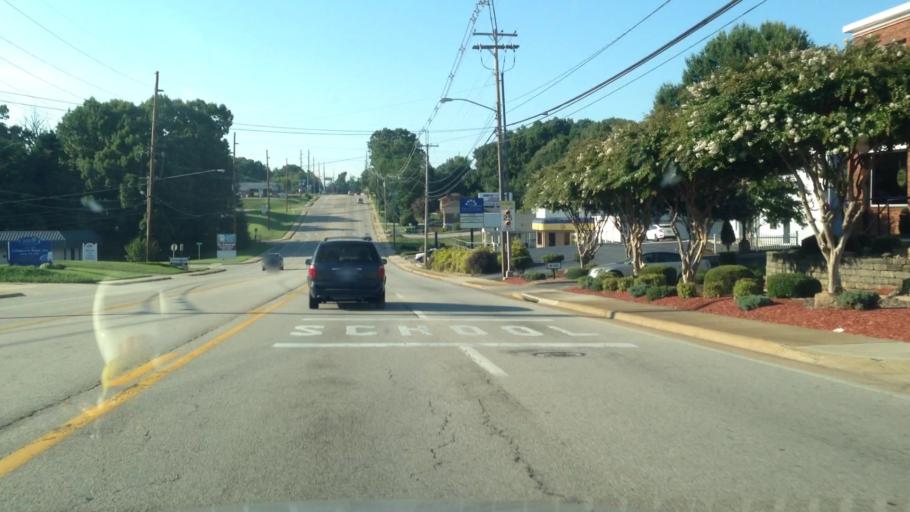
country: US
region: Virginia
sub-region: City of Danville
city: Danville
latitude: 36.6129
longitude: -79.4056
